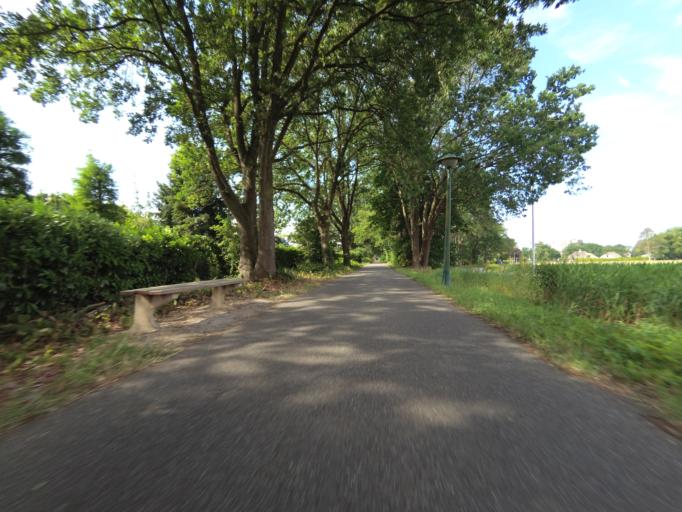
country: NL
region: Overijssel
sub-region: Gemeente Enschede
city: Enschede
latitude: 52.2443
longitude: 6.9065
